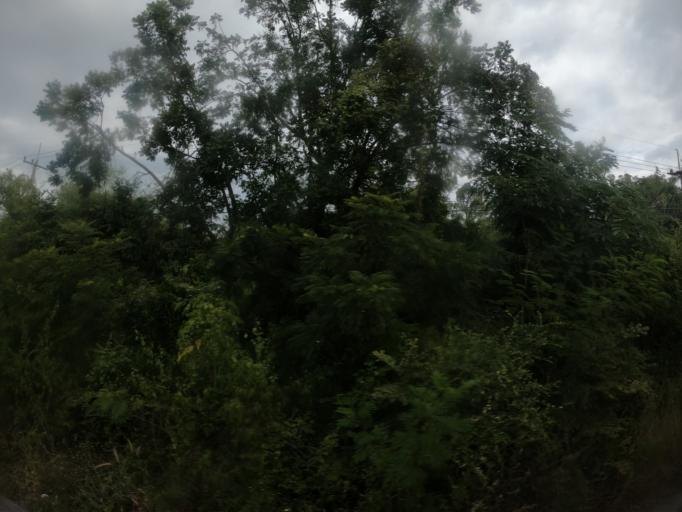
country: TH
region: Maha Sarakham
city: Kantharawichai
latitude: 16.3323
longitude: 103.2396
